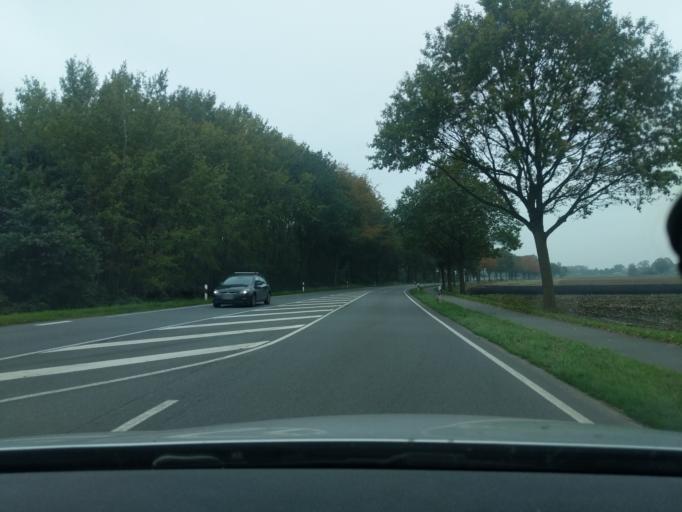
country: DE
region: Lower Saxony
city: Burweg
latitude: 53.6135
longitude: 9.2831
